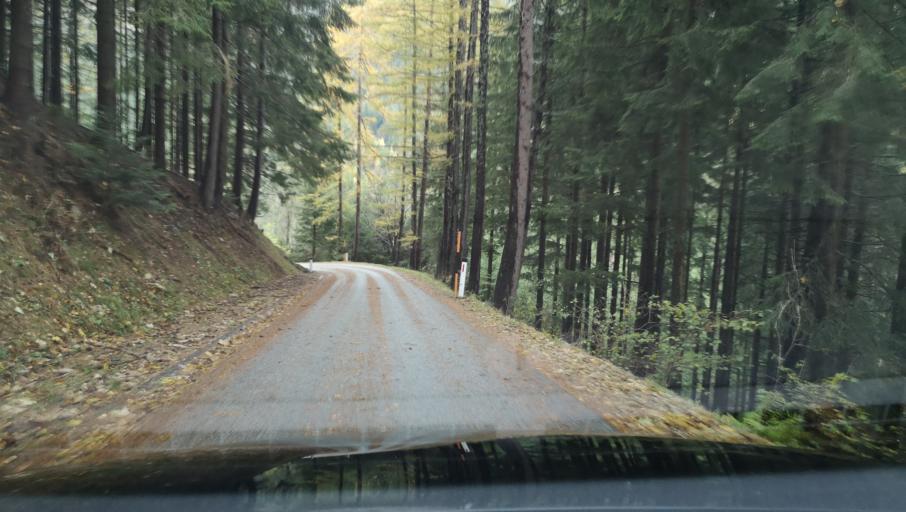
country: AT
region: Styria
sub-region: Politischer Bezirk Weiz
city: Birkfeld
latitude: 47.3662
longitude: 15.6256
